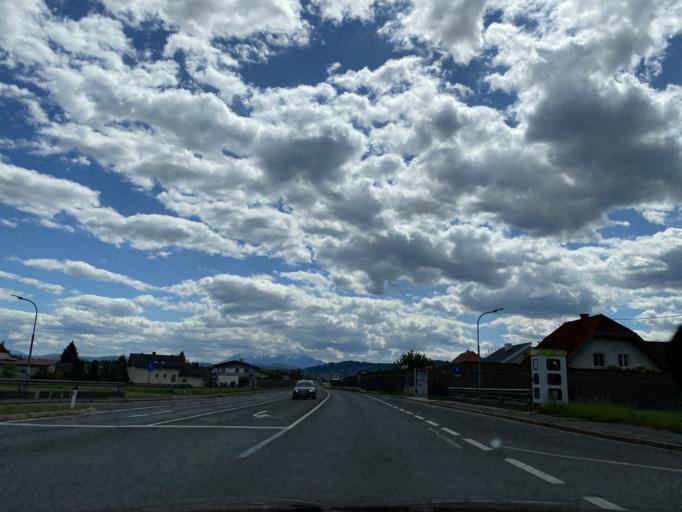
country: AT
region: Carinthia
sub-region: Politischer Bezirk Wolfsberg
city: Wolfsberg
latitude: 46.8097
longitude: 14.8316
